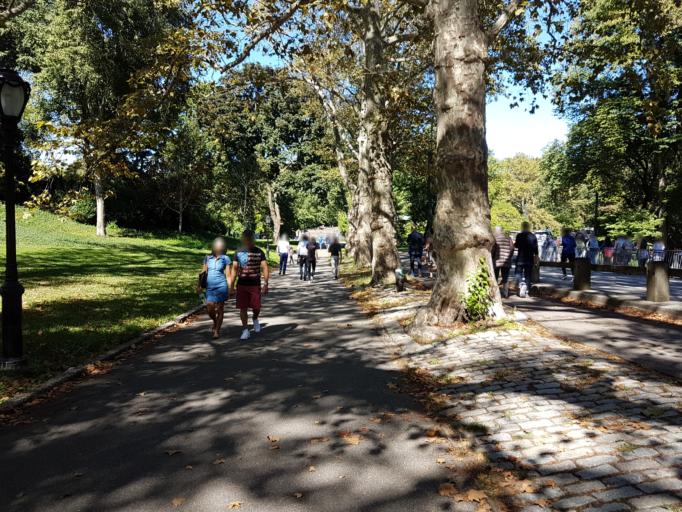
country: US
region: New York
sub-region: New York County
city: Manhattan
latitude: 40.7739
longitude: -73.9693
